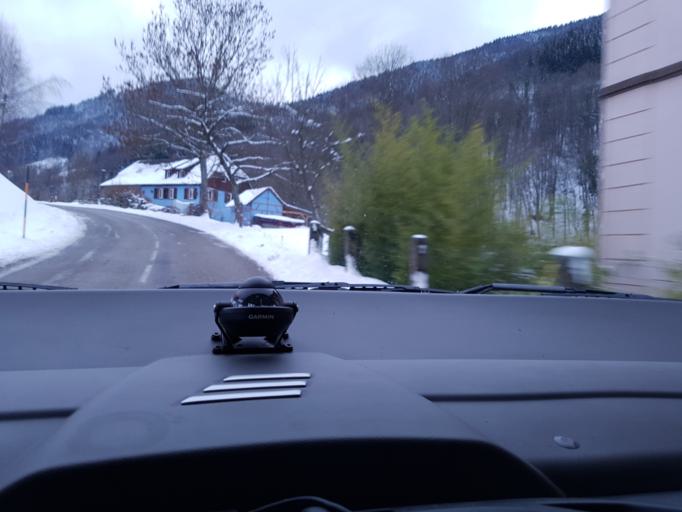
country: FR
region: Alsace
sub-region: Departement du Haut-Rhin
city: Sainte-Marie-aux-Mines
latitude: 48.2144
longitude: 7.1386
